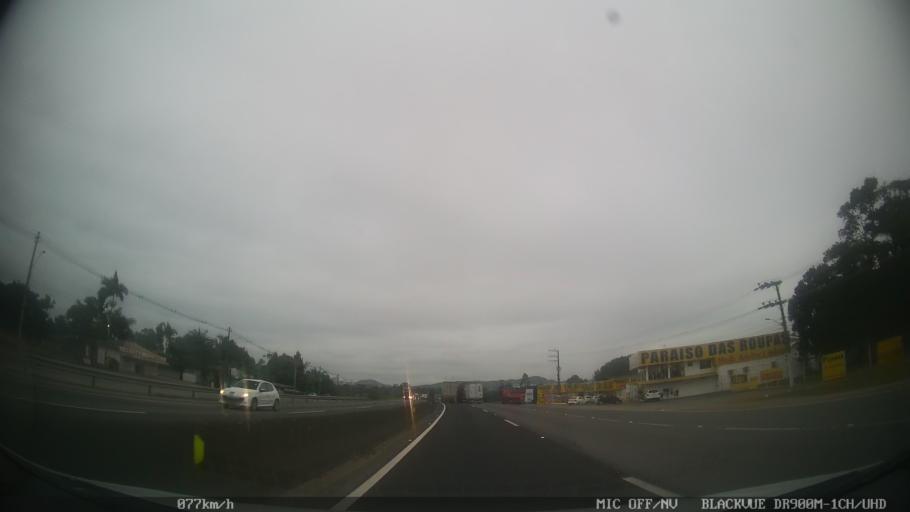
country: BR
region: Santa Catarina
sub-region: Penha
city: Penha
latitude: -26.7483
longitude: -48.6956
